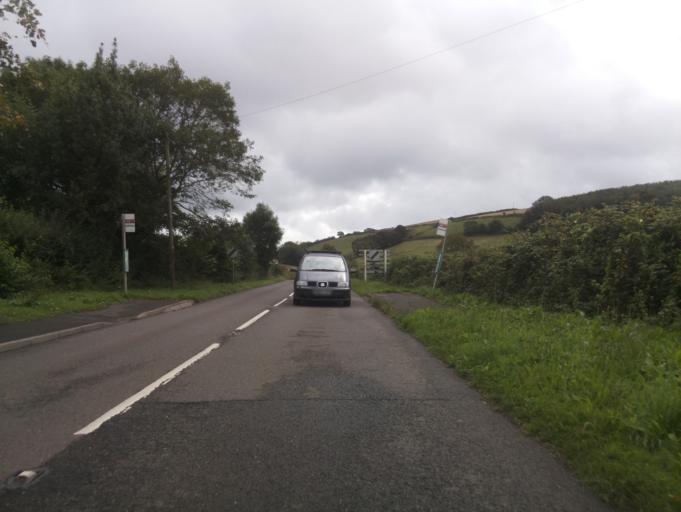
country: GB
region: England
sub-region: Devon
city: Salcombe
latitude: 50.2727
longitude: -3.6740
